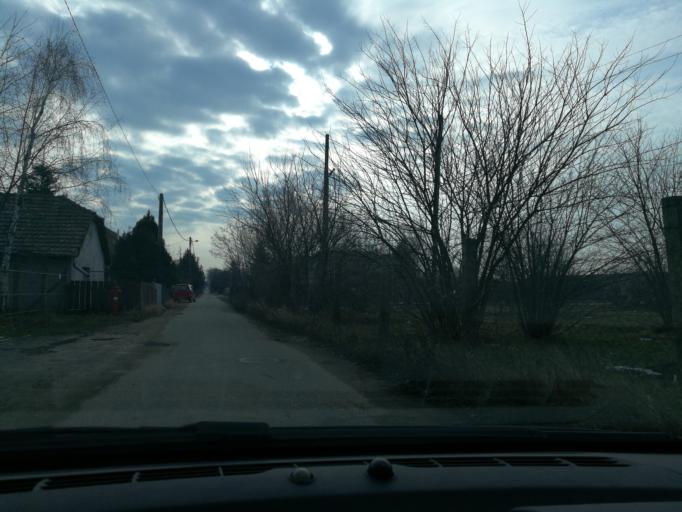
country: HU
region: Szabolcs-Szatmar-Bereg
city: Nyiregyhaza
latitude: 47.9317
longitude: 21.7215
